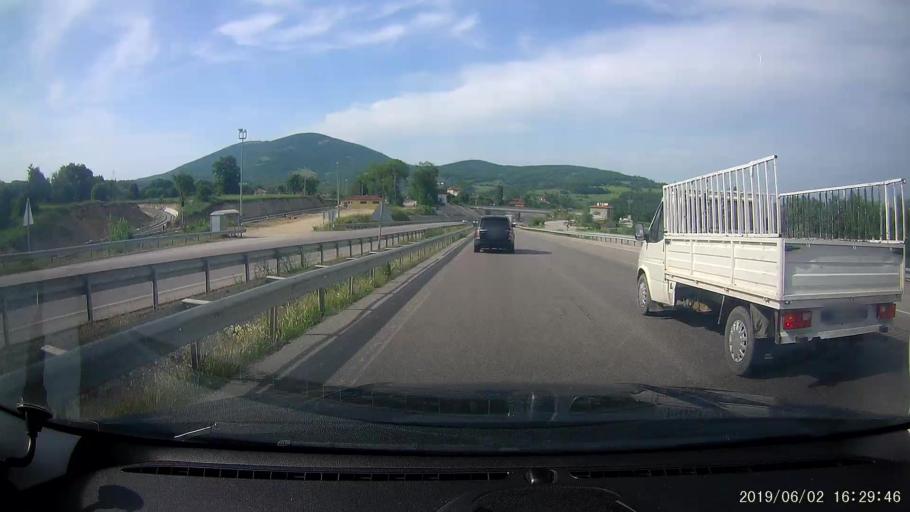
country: TR
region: Samsun
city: Ladik
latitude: 41.0170
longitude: 35.8723
